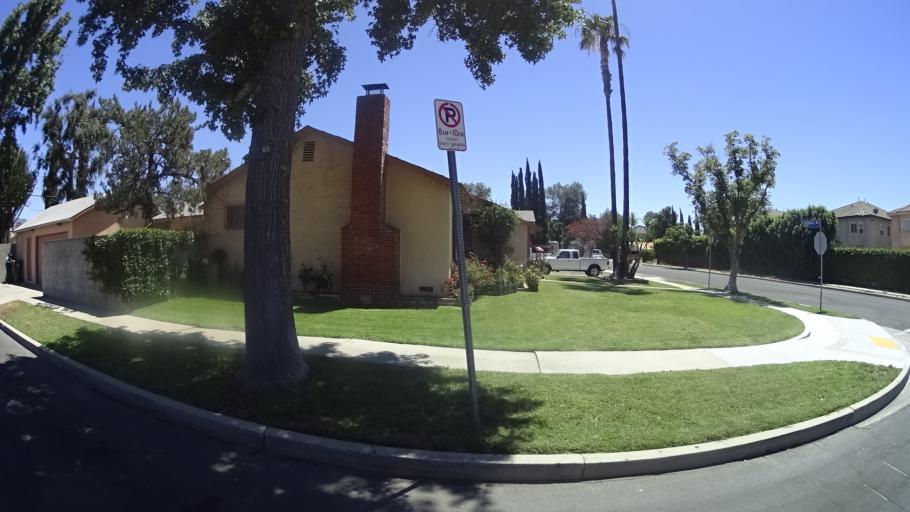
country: US
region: California
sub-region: Los Angeles County
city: San Fernando
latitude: 34.2511
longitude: -118.4697
